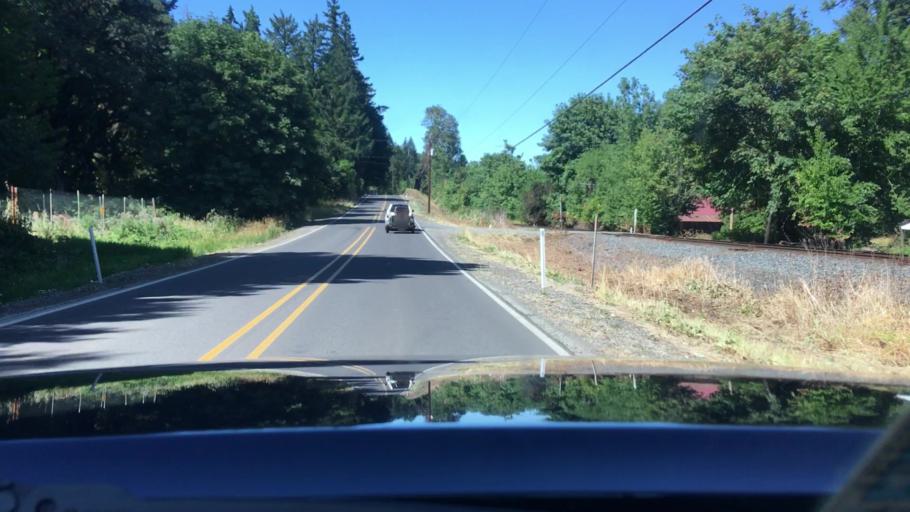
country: US
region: Oregon
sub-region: Lane County
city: Cottage Grove
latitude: 43.8165
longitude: -123.0458
